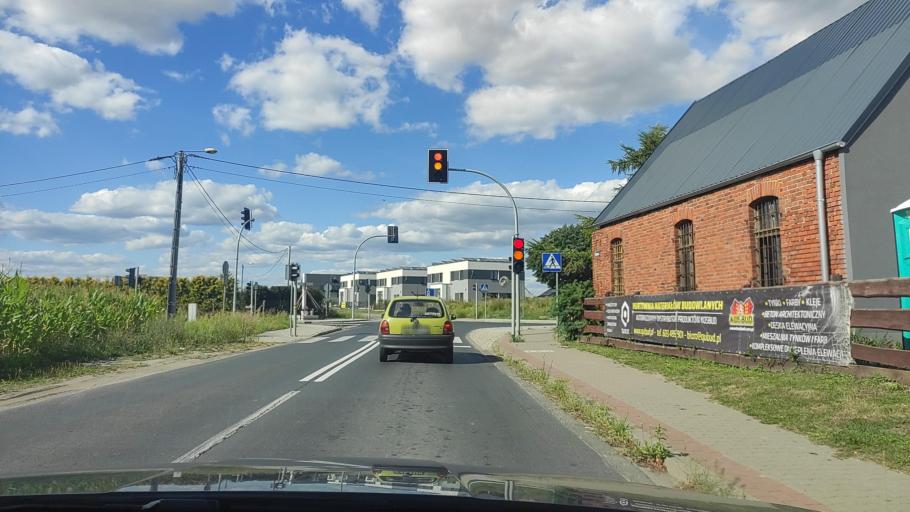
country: PL
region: Greater Poland Voivodeship
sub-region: Powiat poznanski
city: Kleszczewo
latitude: 52.3560
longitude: 17.1723
